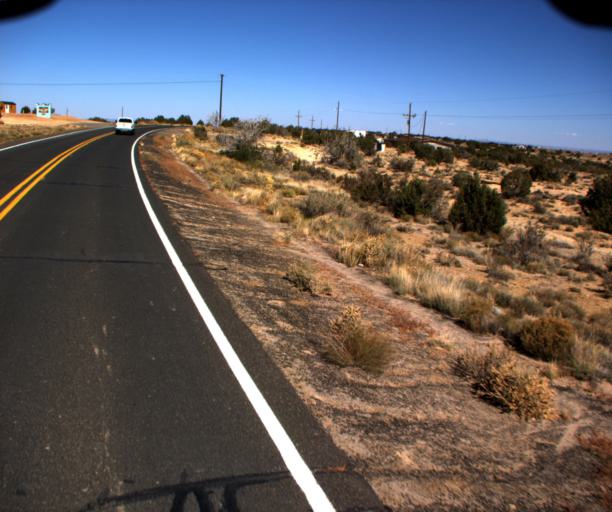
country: US
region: Arizona
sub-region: Navajo County
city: First Mesa
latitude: 35.8271
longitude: -110.5325
